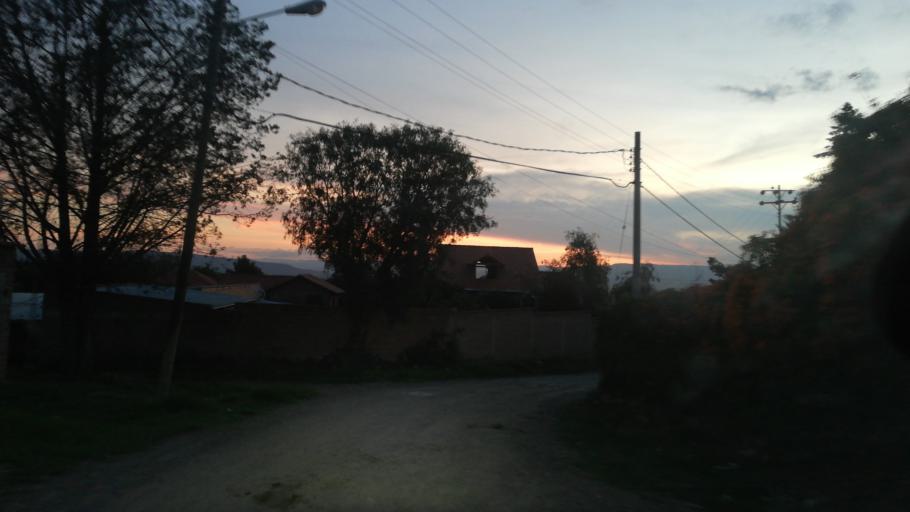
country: BO
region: Cochabamba
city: Cochabamba
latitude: -17.3305
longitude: -66.2061
